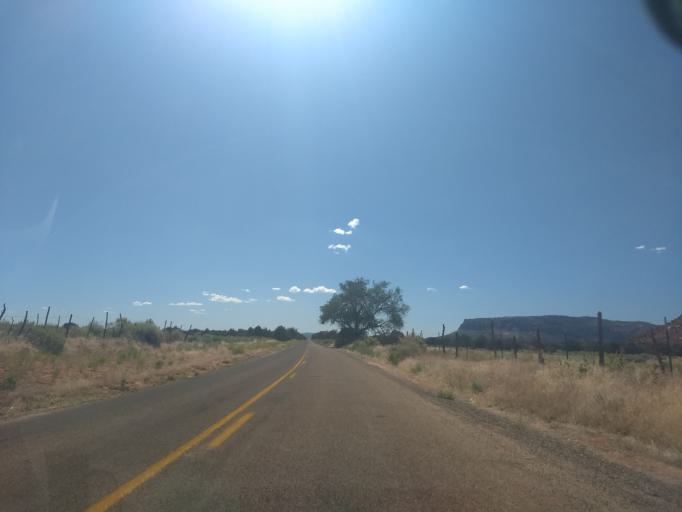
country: US
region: Utah
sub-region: Washington County
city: Hildale
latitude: 36.9468
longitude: -112.8751
